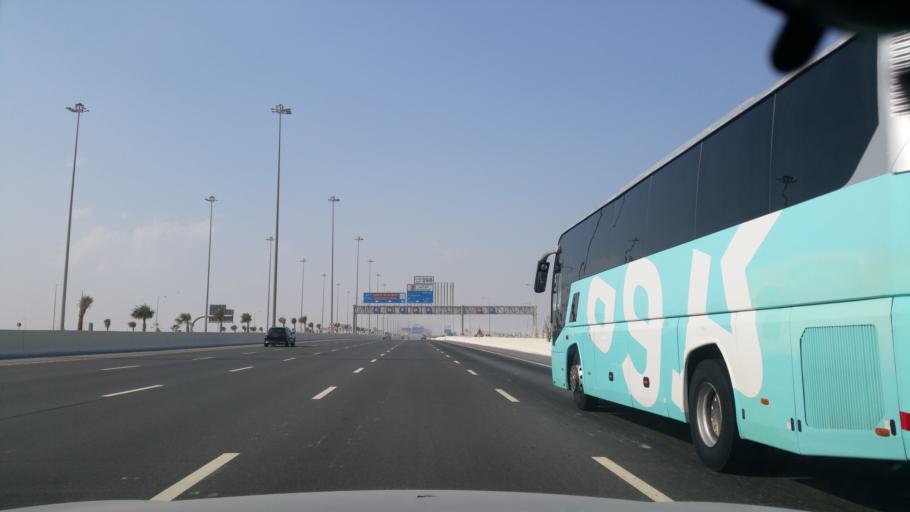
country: QA
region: Baladiyat Umm Salal
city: Umm Salal Muhammad
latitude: 25.4334
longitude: 51.4838
